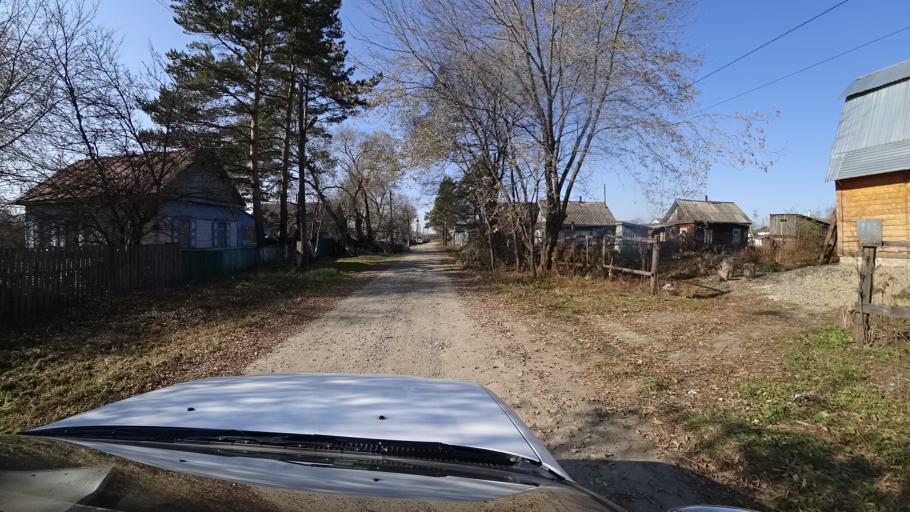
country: RU
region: Primorskiy
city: Dal'nerechensk
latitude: 45.9286
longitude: 133.7155
